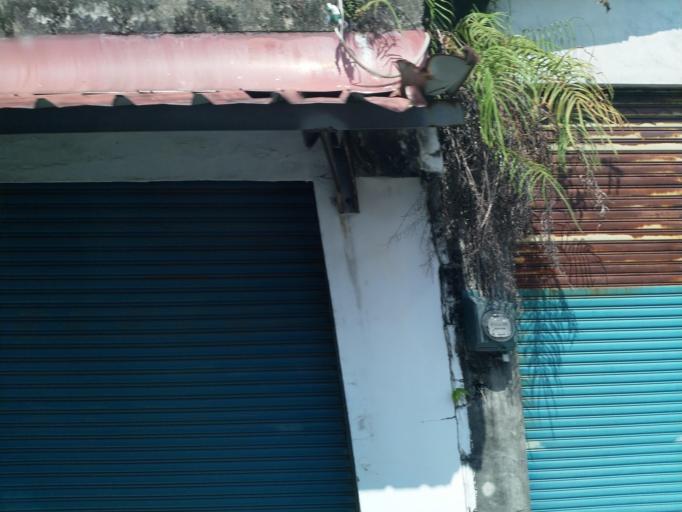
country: TW
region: Taiwan
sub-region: Pingtung
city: Pingtung
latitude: 22.8800
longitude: 120.5637
